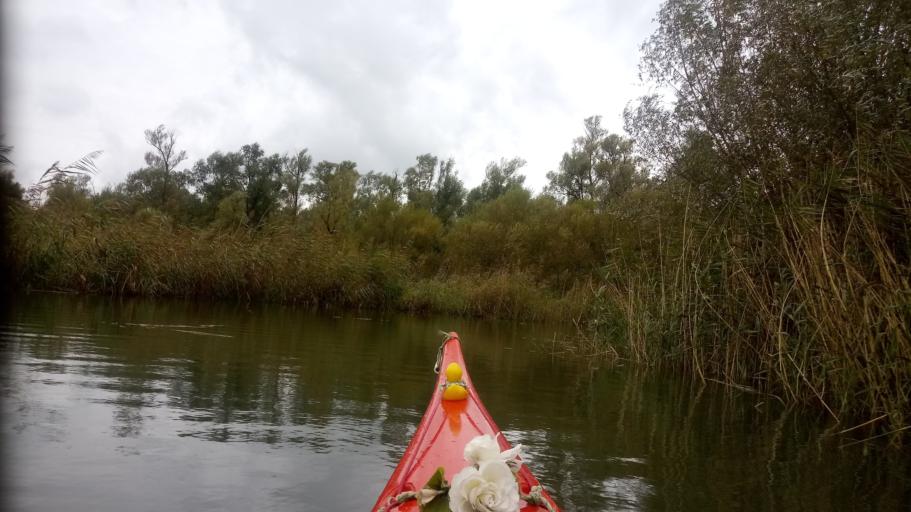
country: NL
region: North Brabant
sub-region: Gemeente Made en Drimmelen
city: Drimmelen
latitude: 51.7525
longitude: 4.7658
